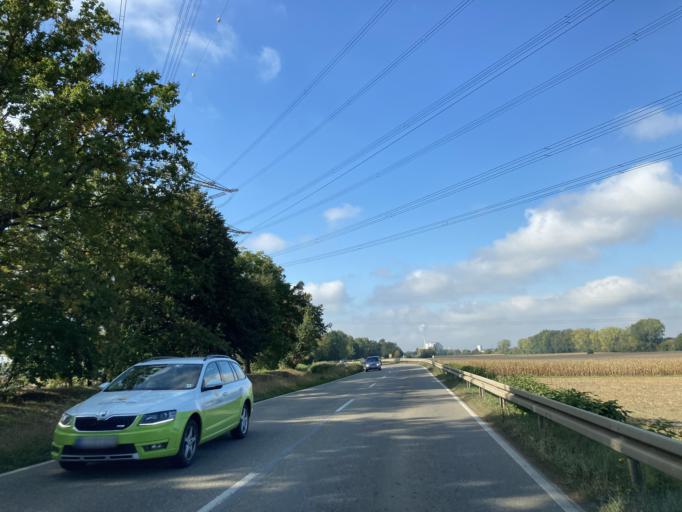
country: DE
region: Baden-Wuerttemberg
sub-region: Freiburg Region
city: Eschbach
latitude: 47.8818
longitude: 7.6386
